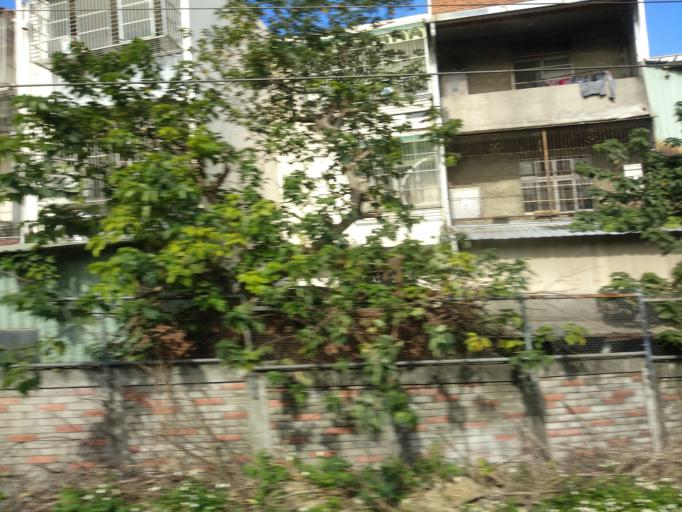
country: TW
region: Taiwan
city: Taoyuan City
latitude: 24.9693
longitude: 121.2519
